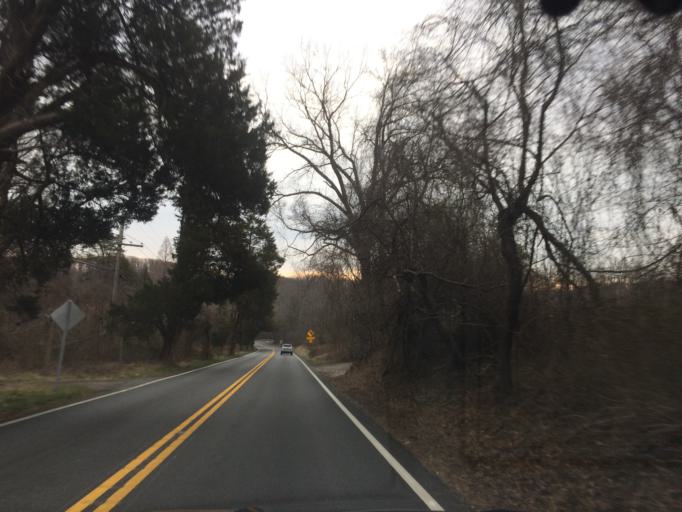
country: US
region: Maryland
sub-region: Montgomery County
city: Ashton-Sandy Spring
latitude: 39.1602
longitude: -76.9789
